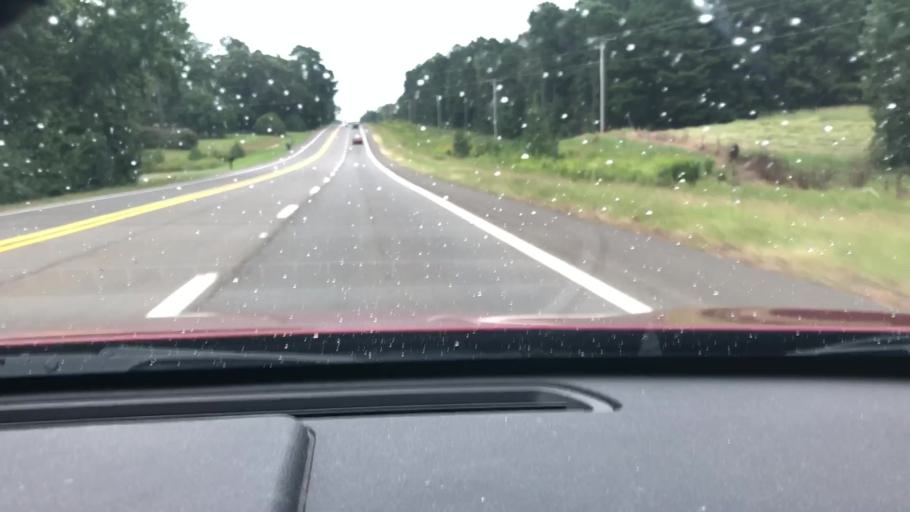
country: US
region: Arkansas
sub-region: Columbia County
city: Waldo
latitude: 33.3512
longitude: -93.3805
